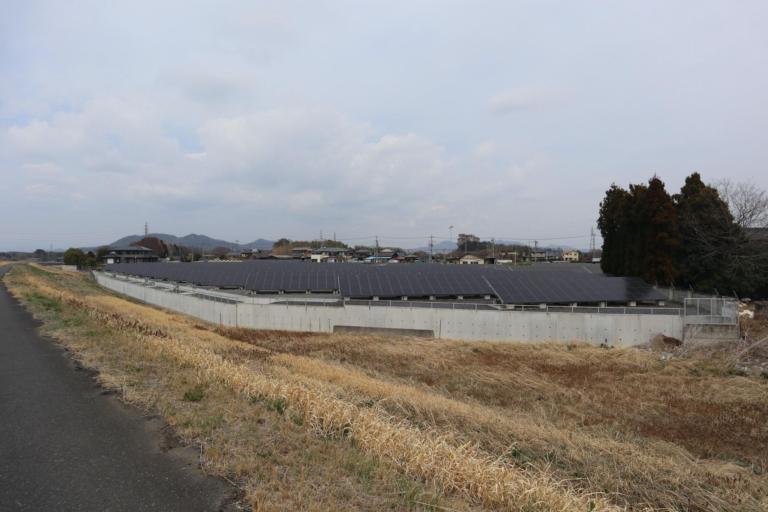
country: JP
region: Tochigi
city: Fujioka
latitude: 36.2683
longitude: 139.6360
